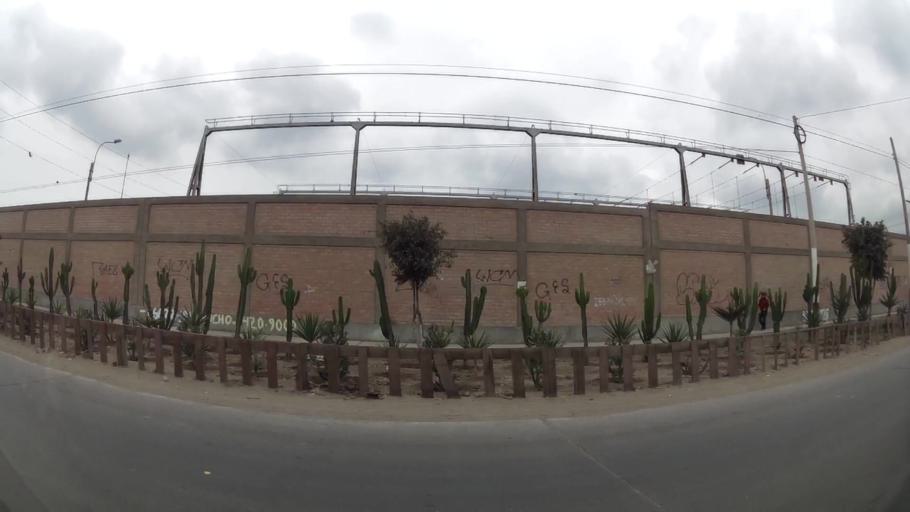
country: PE
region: Callao
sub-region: Callao
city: Callao
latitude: -12.0489
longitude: -77.1046
